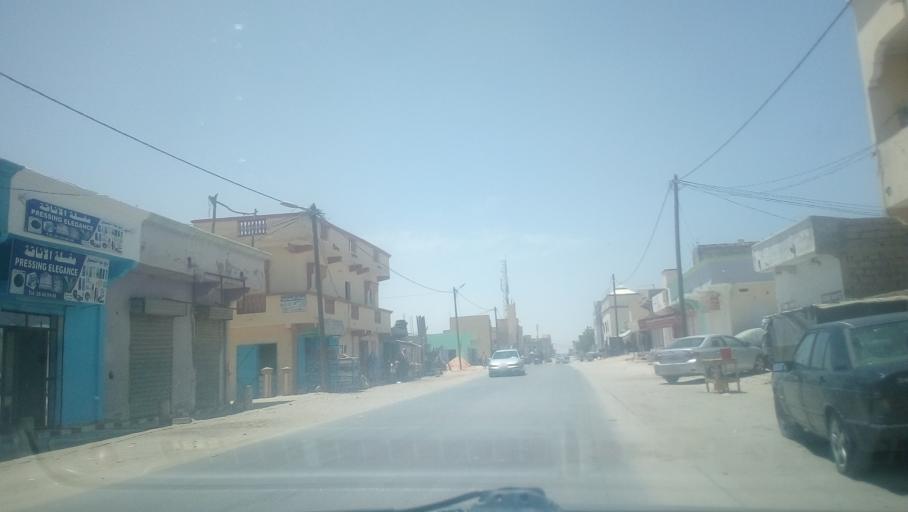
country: MR
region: Nouakchott
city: Nouakchott
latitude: 18.0642
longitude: -15.9594
